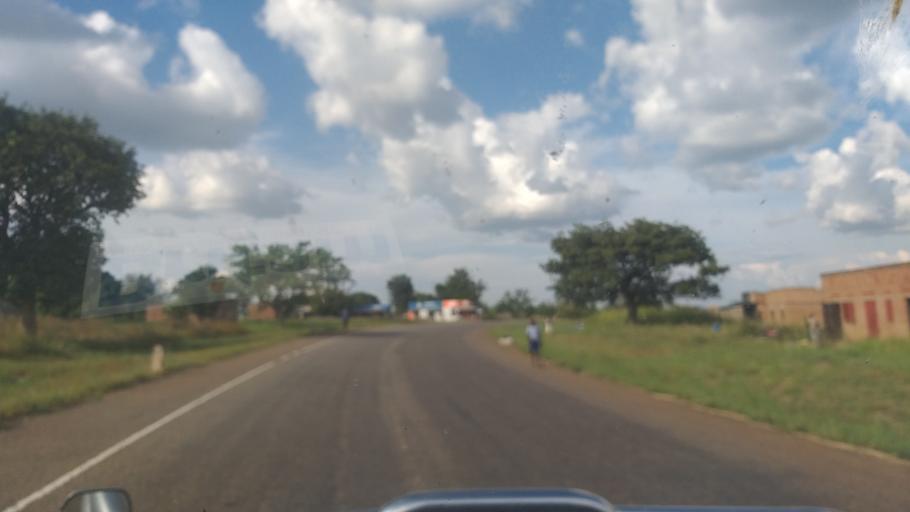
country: UG
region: Northern Region
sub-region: Nebbi District
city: Nebbi
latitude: 2.5612
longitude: 31.1010
